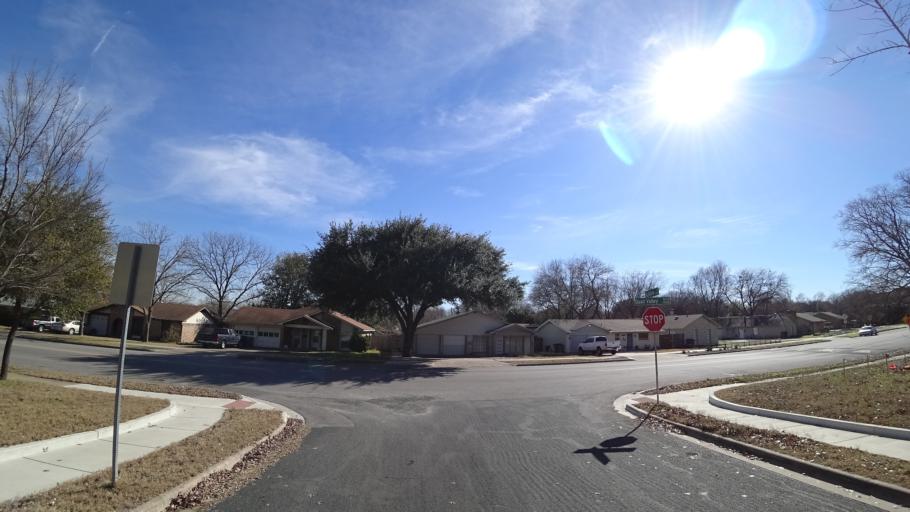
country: US
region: Texas
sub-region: Travis County
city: Wells Branch
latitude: 30.3777
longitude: -97.7090
